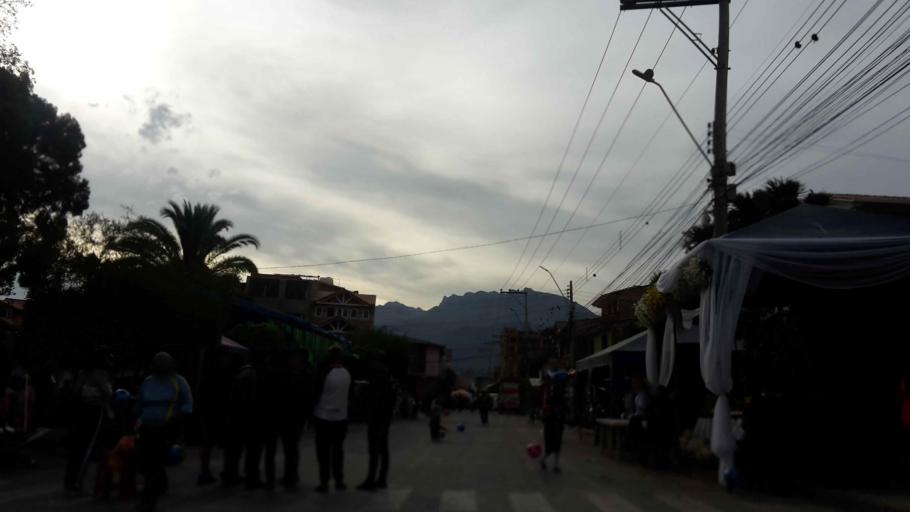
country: BO
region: Cochabamba
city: Cochabamba
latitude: -17.3380
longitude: -66.2182
